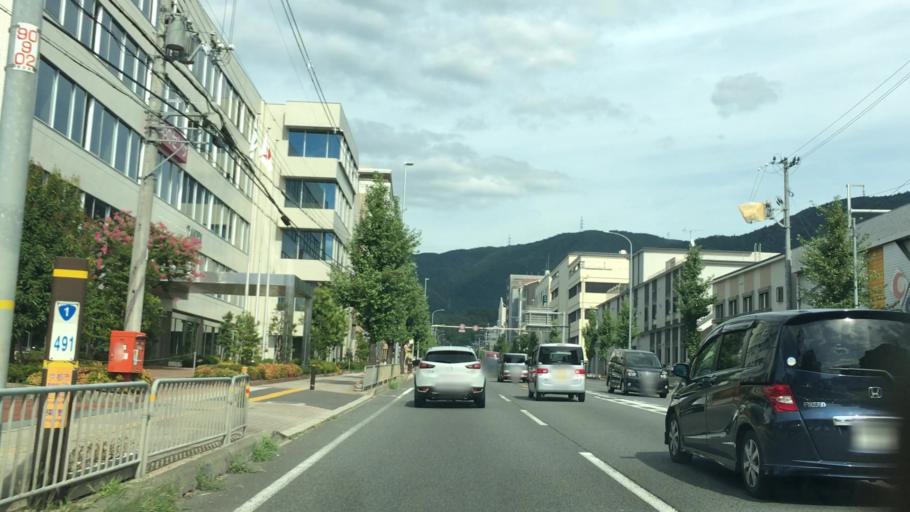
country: JP
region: Shiga Prefecture
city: Otsu-shi
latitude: 34.9813
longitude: 135.8179
